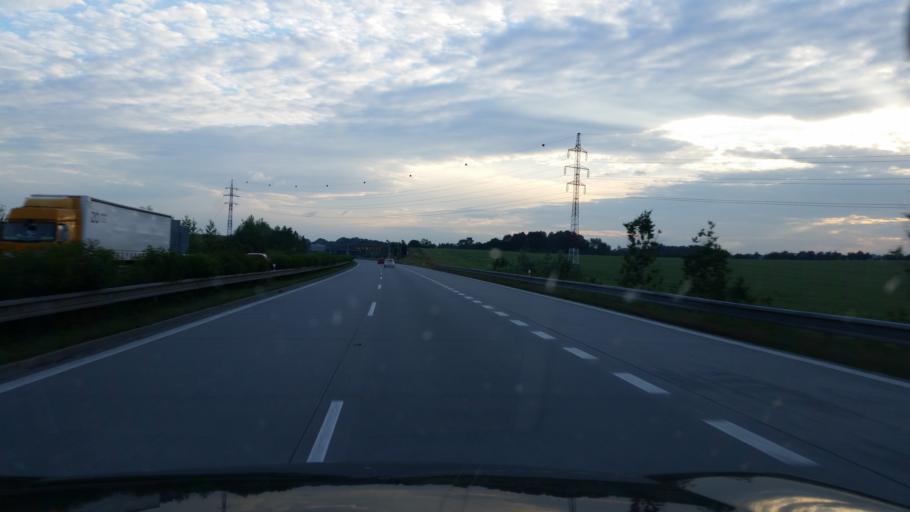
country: CZ
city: Klimkovice
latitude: 49.7996
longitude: 18.1381
